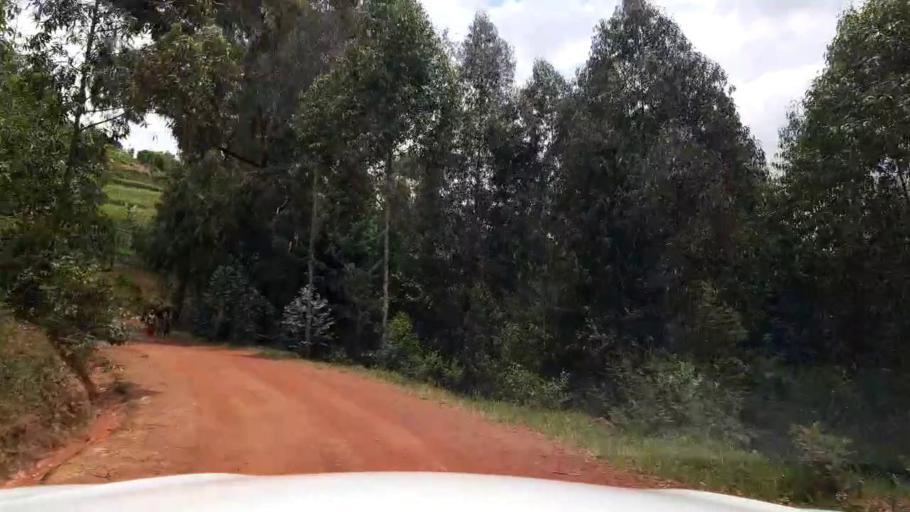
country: RW
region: Northern Province
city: Byumba
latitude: -1.5118
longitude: 29.9405
